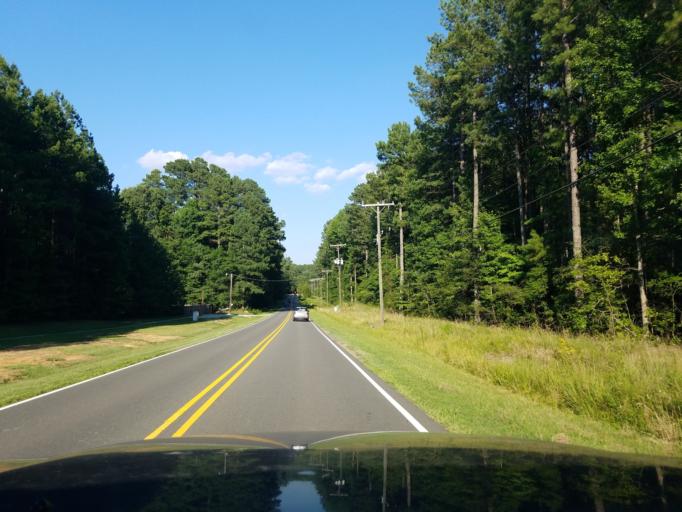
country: US
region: North Carolina
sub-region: Wake County
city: Green Level
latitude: 35.8755
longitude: -78.9200
